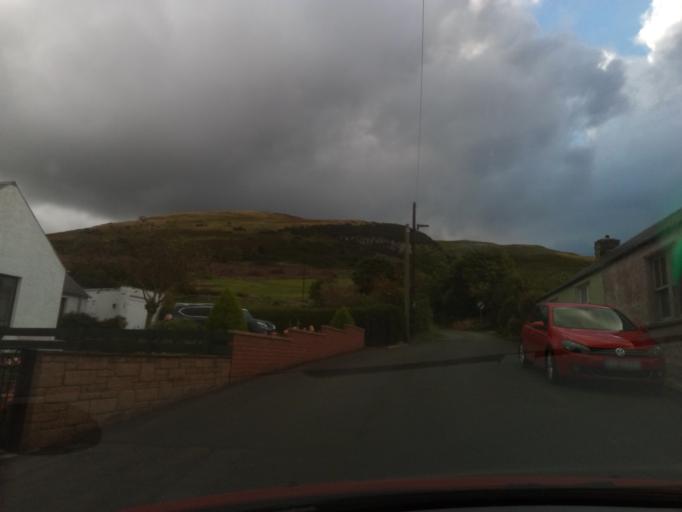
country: GB
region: Scotland
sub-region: The Scottish Borders
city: Coldstream
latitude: 55.5464
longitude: -2.2742
